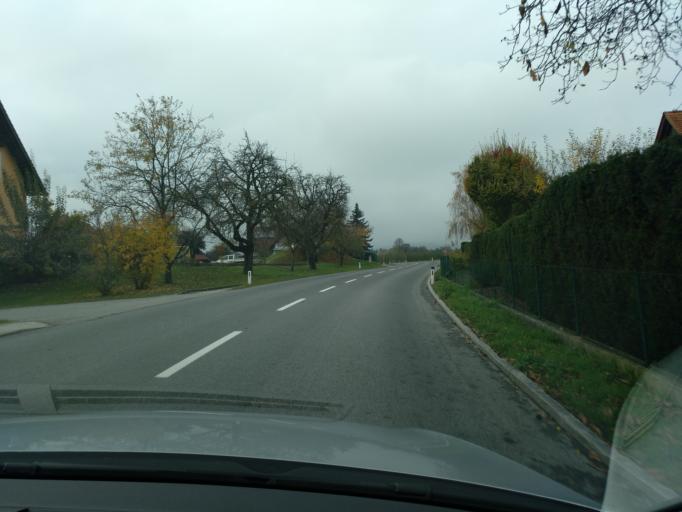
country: AT
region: Styria
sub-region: Politischer Bezirk Hartberg-Fuerstenfeld
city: Rabenwald
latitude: 47.3166
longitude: 15.8131
